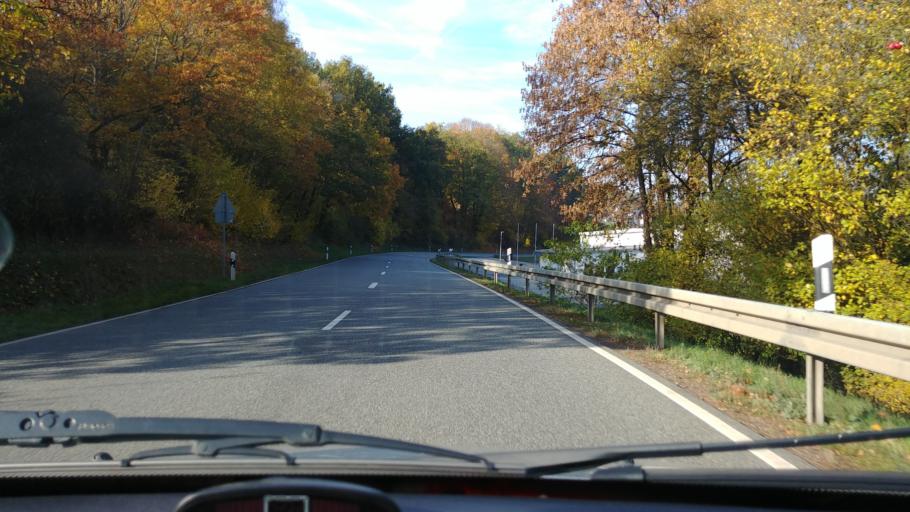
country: DE
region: Rheinland-Pfalz
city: Schiesheim
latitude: 50.2582
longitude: 8.0552
